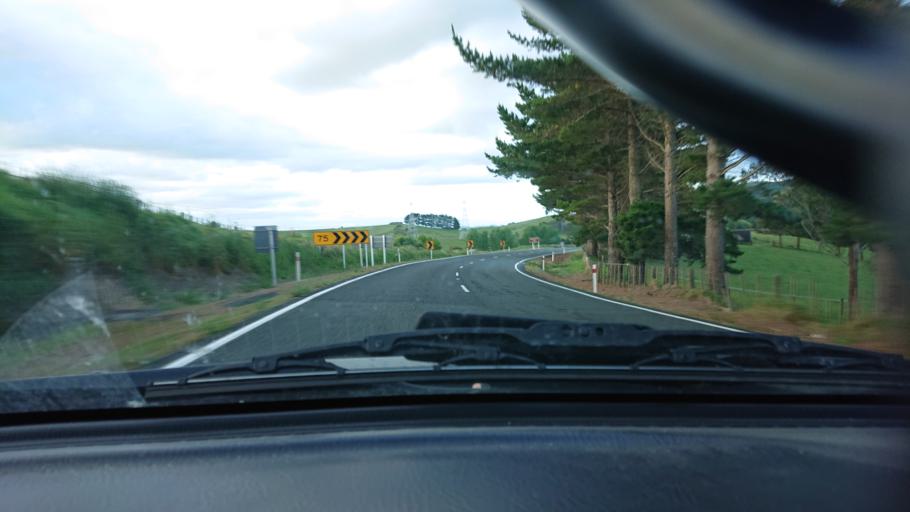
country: NZ
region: Auckland
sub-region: Auckland
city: Parakai
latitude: -36.4686
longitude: 174.4469
